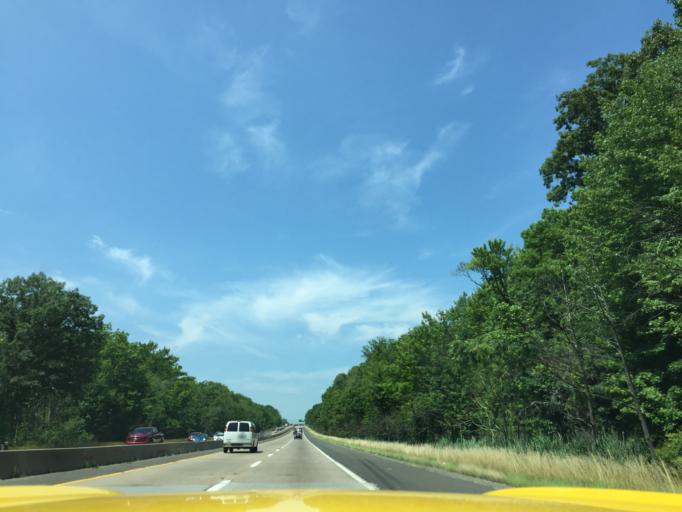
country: US
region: Pennsylvania
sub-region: Bucks County
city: Fairless Hills
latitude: 40.1938
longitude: -74.8490
